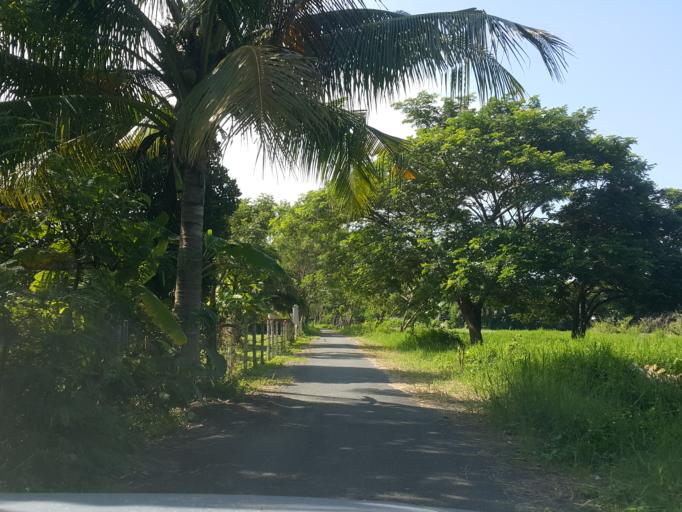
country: TH
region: Chiang Mai
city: Saraphi
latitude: 18.7317
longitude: 99.0435
